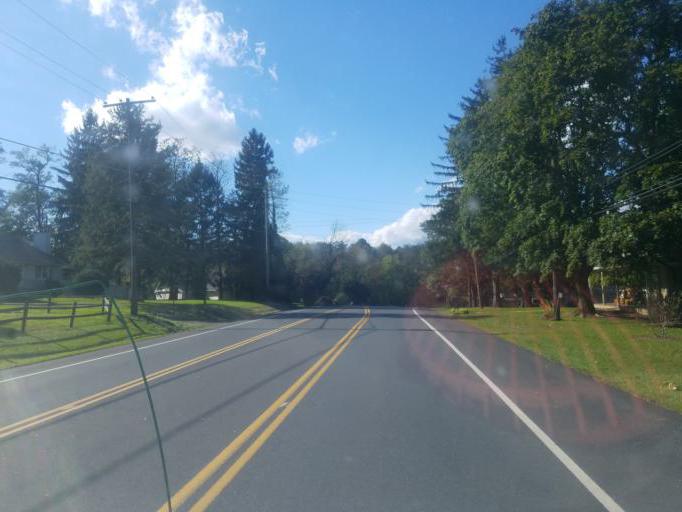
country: US
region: Pennsylvania
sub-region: Dauphin County
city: Middletown
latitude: 40.1923
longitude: -76.6903
